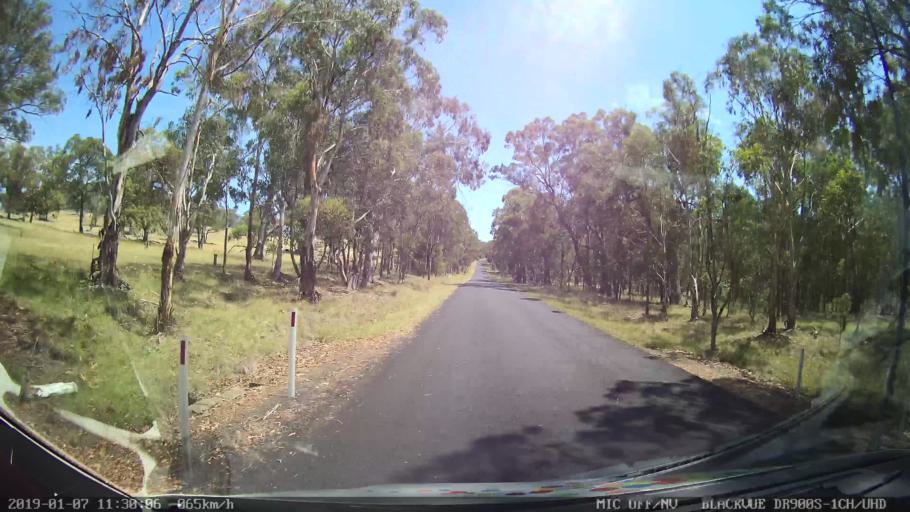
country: AU
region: New South Wales
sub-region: Armidale Dumaresq
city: Armidale
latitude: -30.4325
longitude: 151.5642
